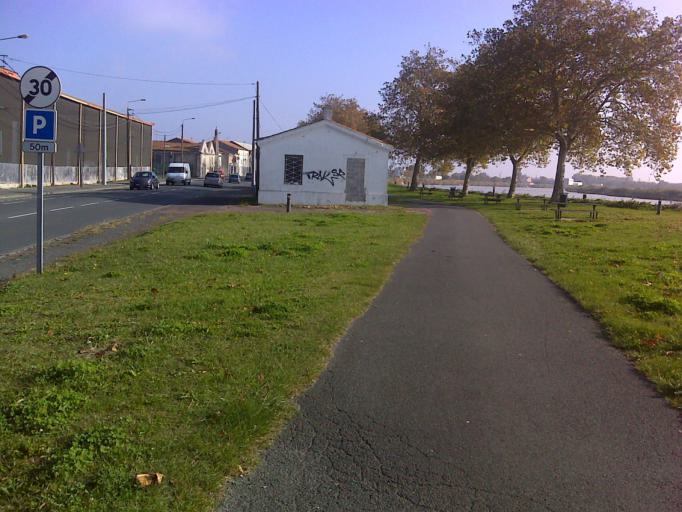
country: FR
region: Poitou-Charentes
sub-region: Departement de la Charente-Maritime
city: Rochefort
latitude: 45.9473
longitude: -0.9526
